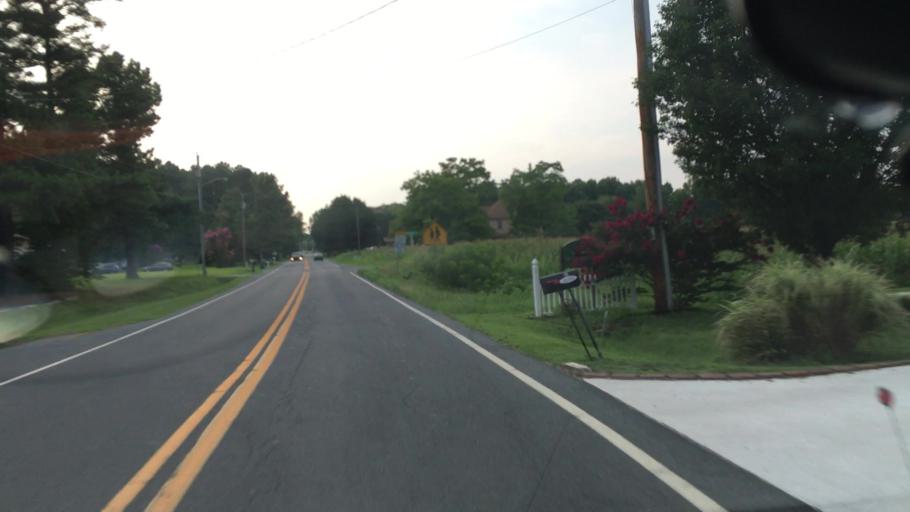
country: US
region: Delaware
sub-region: Sussex County
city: Ocean View
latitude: 38.5428
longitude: -75.1017
